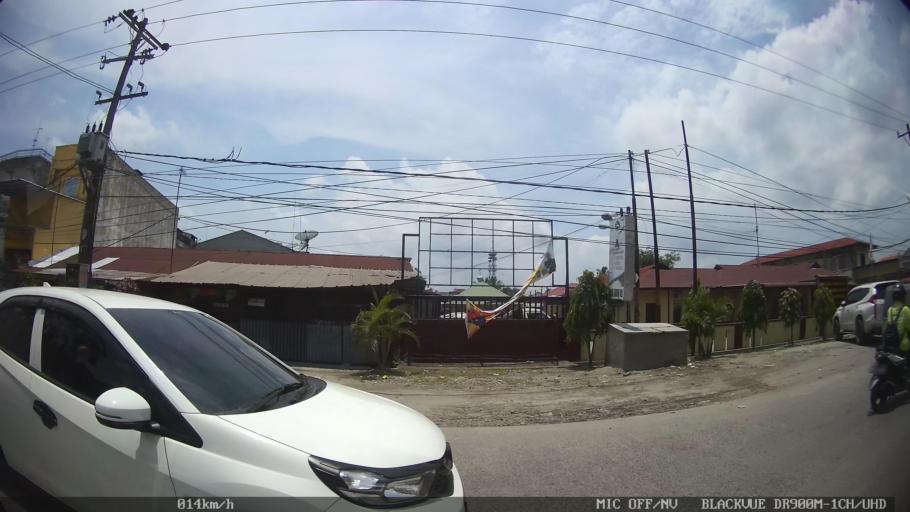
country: ID
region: North Sumatra
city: Labuhan Deli
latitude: 3.7233
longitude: 98.6782
